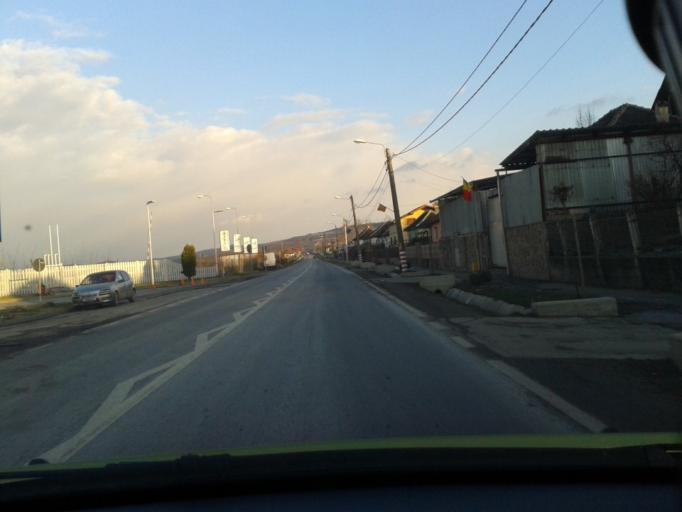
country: RO
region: Sibiu
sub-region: Comuna Copsa Mica
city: Copsa Mica
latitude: 46.1142
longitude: 24.2329
